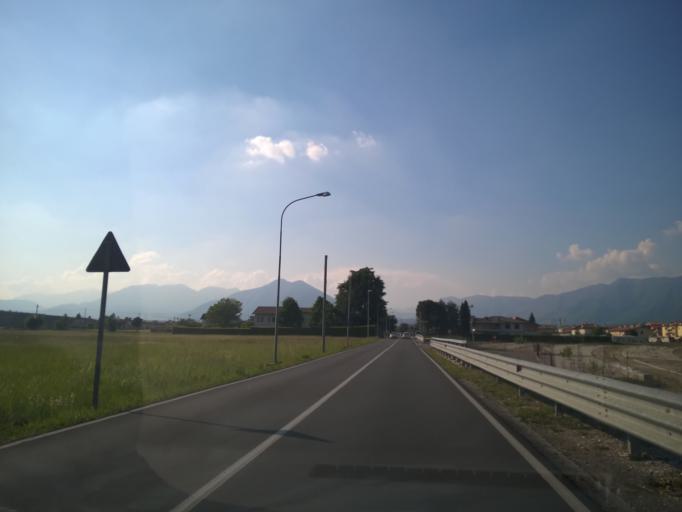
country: IT
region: Veneto
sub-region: Provincia di Vicenza
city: Thiene
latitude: 45.6955
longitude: 11.4947
